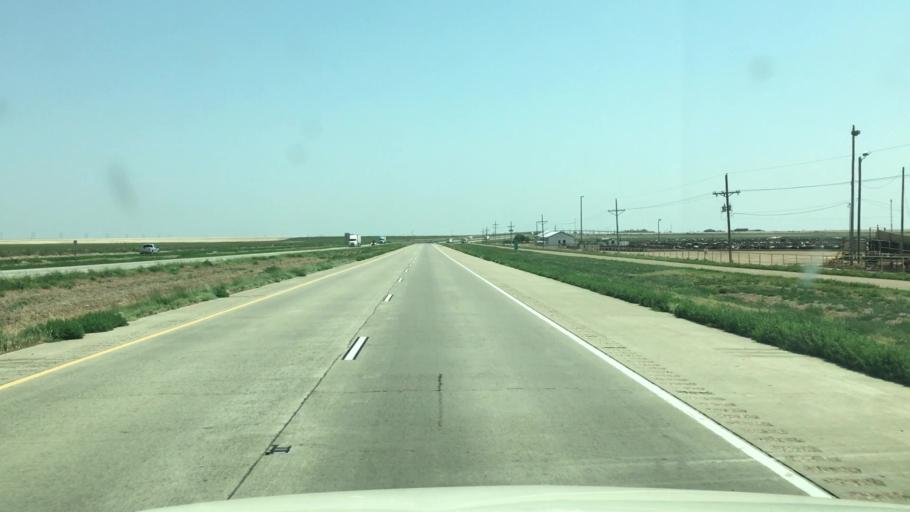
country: US
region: Texas
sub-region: Potter County
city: Bushland
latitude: 35.2088
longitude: -102.1756
